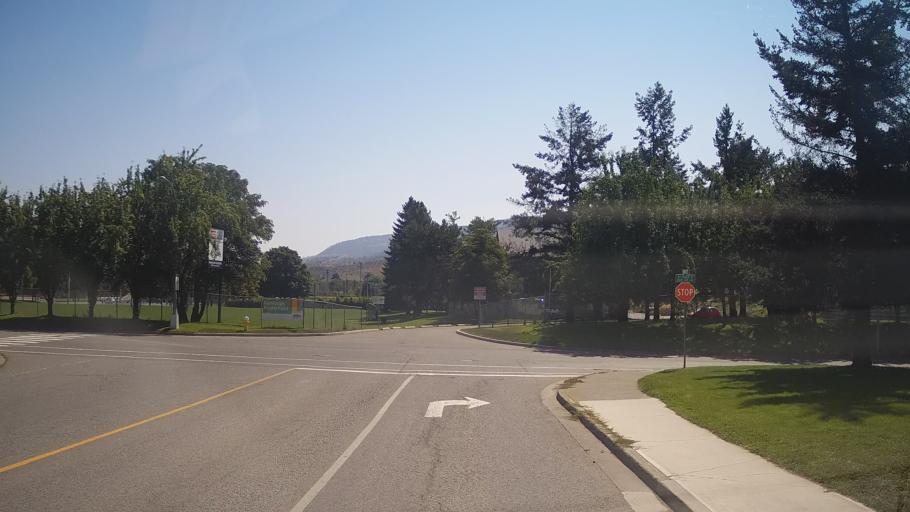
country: CA
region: British Columbia
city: Kamloops
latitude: 50.6755
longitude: -120.3161
